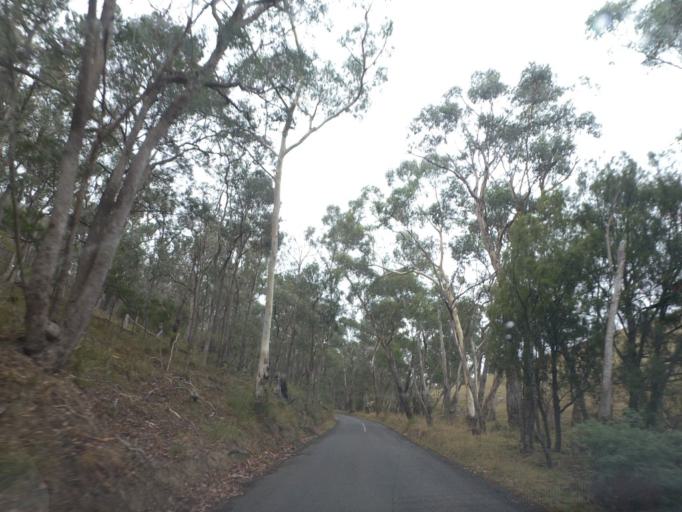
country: AU
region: Victoria
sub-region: Nillumbik
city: Saint Andrews
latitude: -37.6209
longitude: 145.2709
